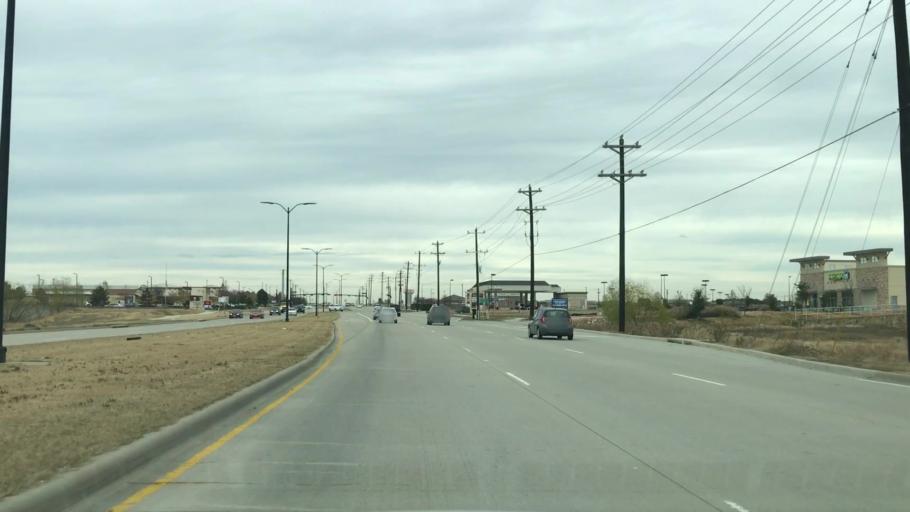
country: US
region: Texas
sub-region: Denton County
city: The Colony
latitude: 33.1231
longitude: -96.8913
